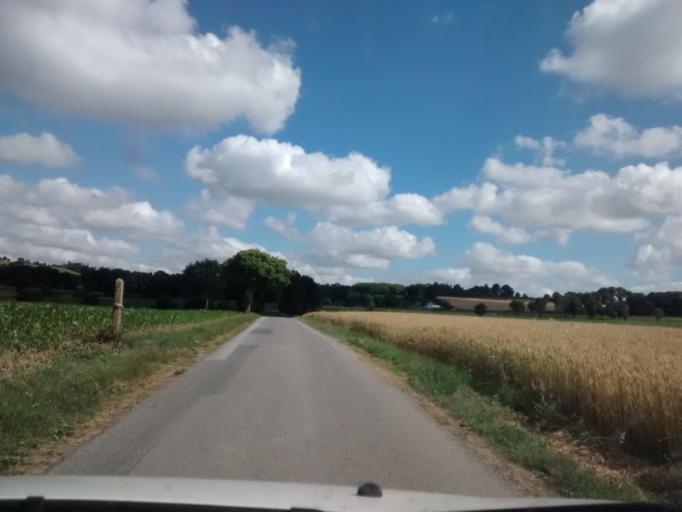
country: FR
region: Brittany
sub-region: Departement d'Ille-et-Vilaine
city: Bain-de-Bretagne
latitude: 47.8384
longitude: -1.7109
